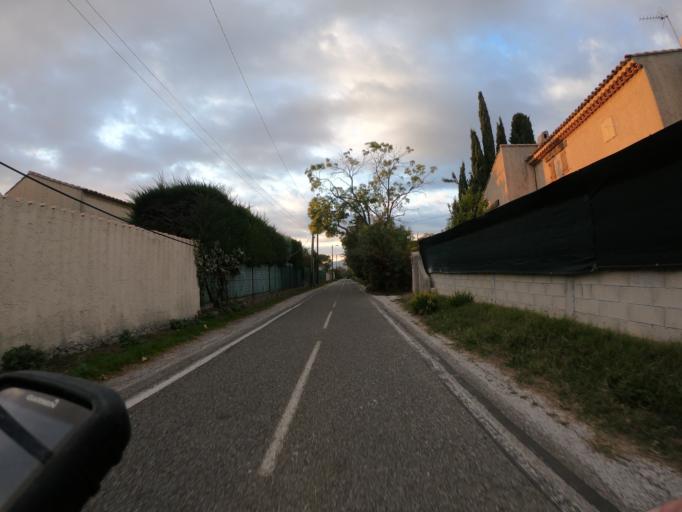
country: FR
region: Provence-Alpes-Cote d'Azur
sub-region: Departement du Var
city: La Garde
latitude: 43.1105
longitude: 5.9971
